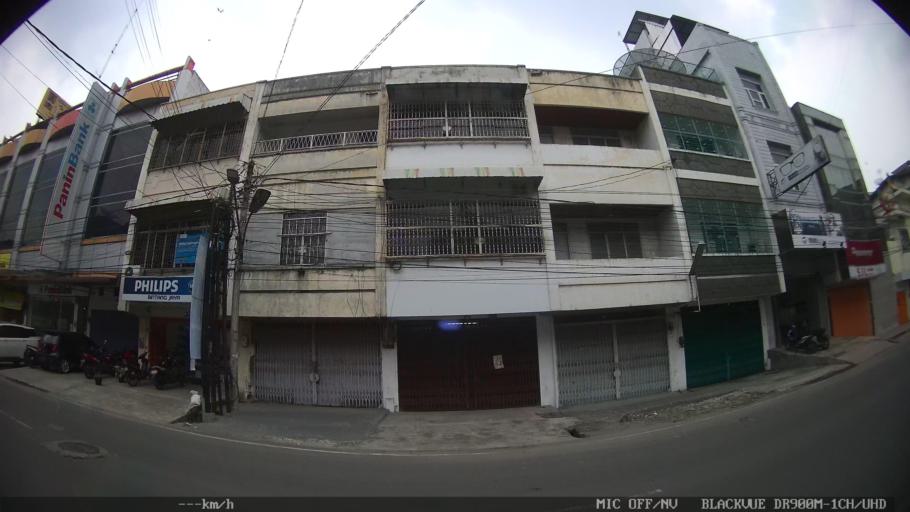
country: ID
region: North Sumatra
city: Medan
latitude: 3.5869
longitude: 98.6962
